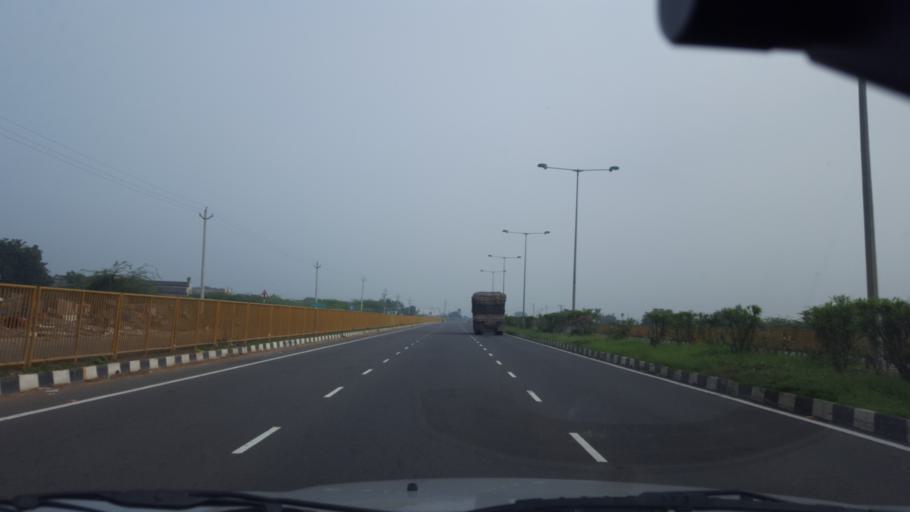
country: IN
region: Andhra Pradesh
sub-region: Guntur
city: Chilakalurupet
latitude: 16.0038
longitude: 80.1132
